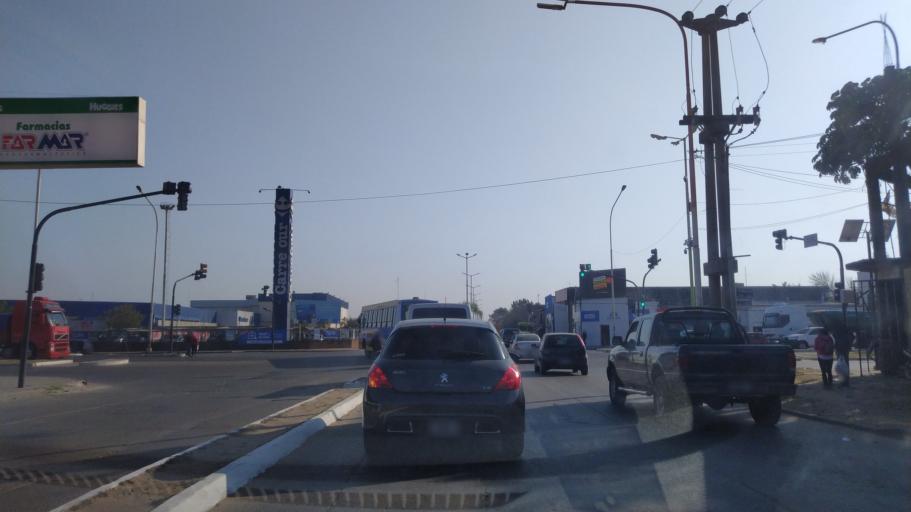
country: AR
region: Corrientes
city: Corrientes
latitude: -27.4789
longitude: -58.8148
